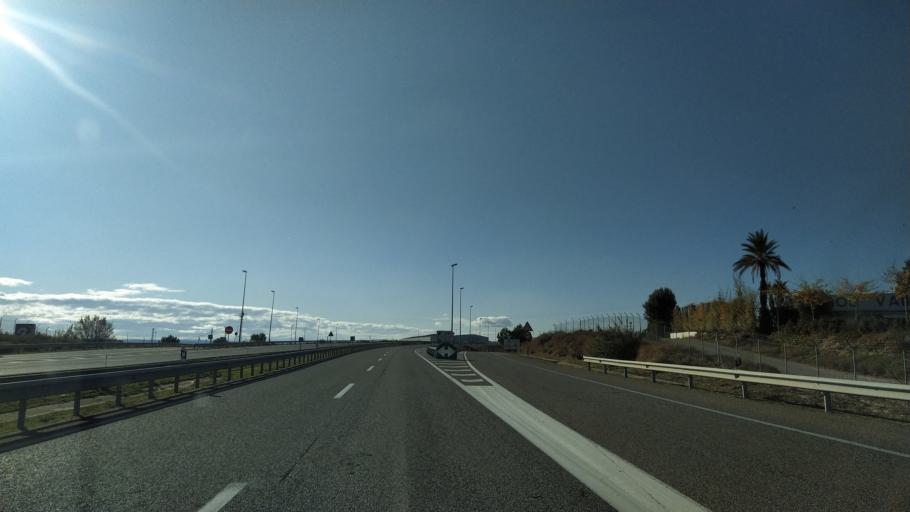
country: ES
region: Catalonia
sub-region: Provincia de Lleida
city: Soses
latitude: 41.5533
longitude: 0.4907
